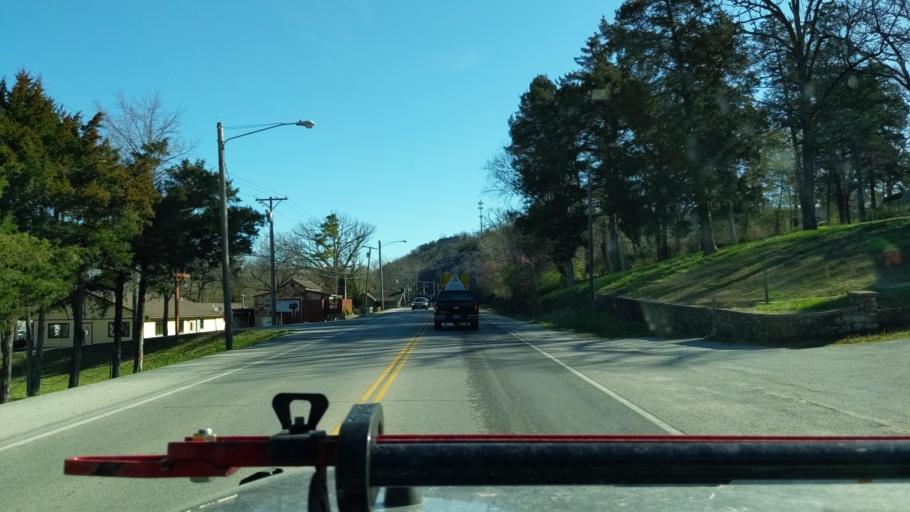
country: US
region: Missouri
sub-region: Taney County
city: Hollister
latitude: 36.6298
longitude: -93.2173
